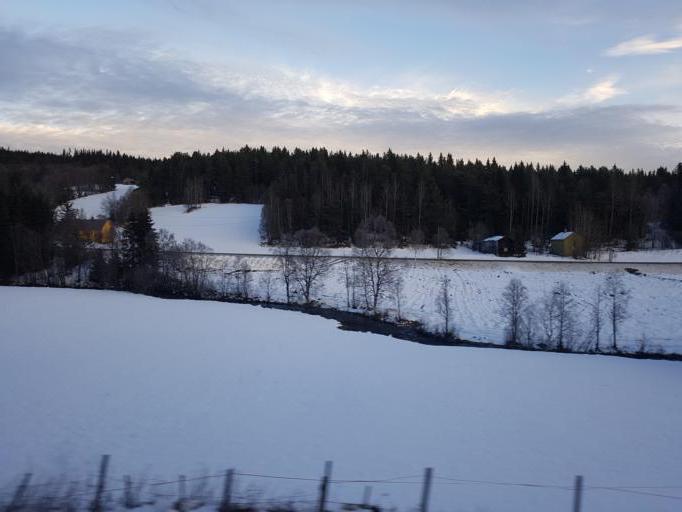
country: NO
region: Sor-Trondelag
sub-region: Rennebu
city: Berkak
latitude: 62.8705
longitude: 10.0577
